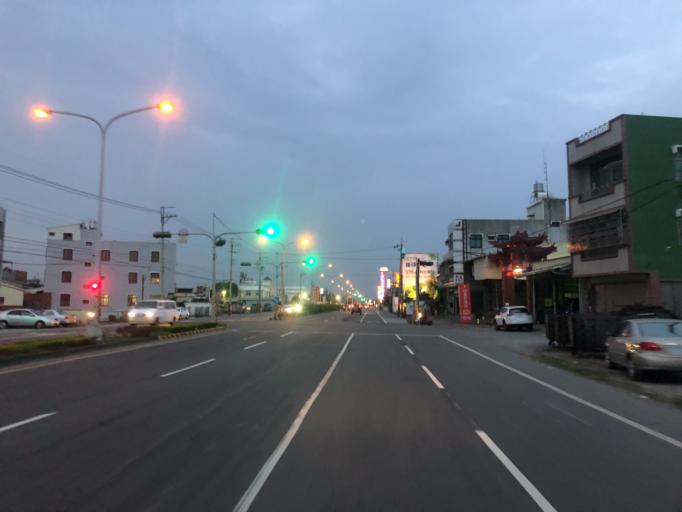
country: TW
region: Taiwan
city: Yujing
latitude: 23.1349
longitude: 120.3219
